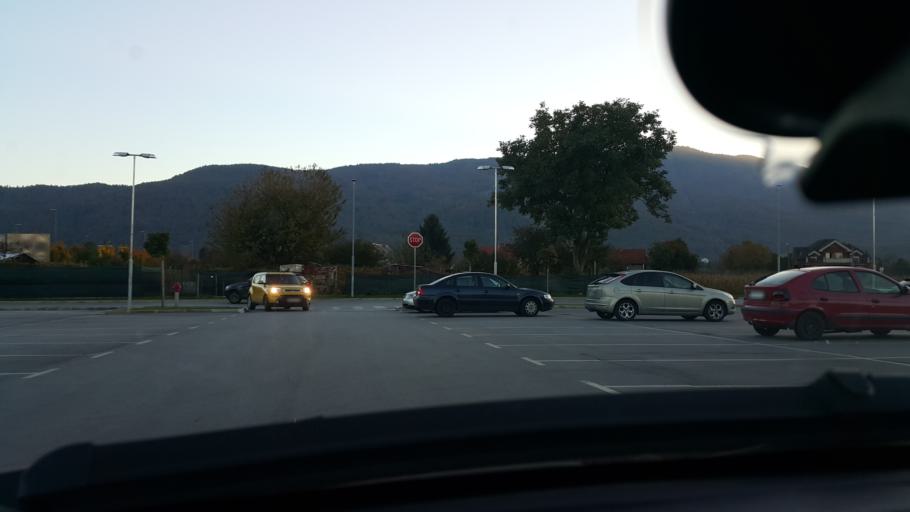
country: SI
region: Maribor
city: Pekre
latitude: 46.5449
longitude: 15.6186
